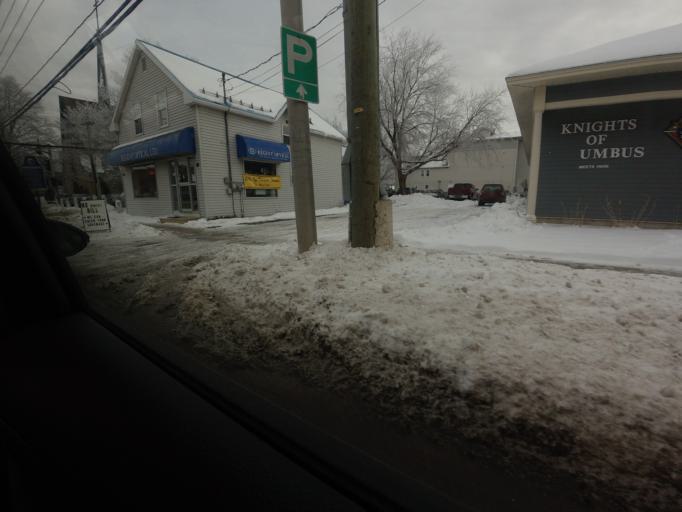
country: CA
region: New Brunswick
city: Fredericton
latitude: 45.9589
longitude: -66.6405
